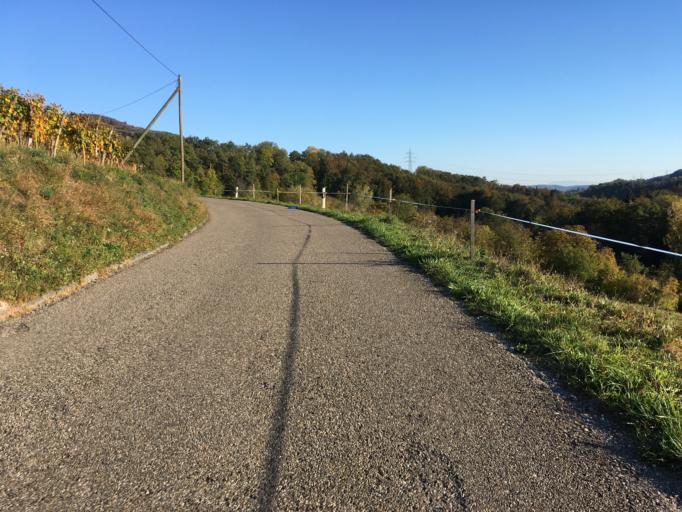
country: CH
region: Zurich
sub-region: Bezirk Buelach
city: Rorbas
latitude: 47.5495
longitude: 8.5601
